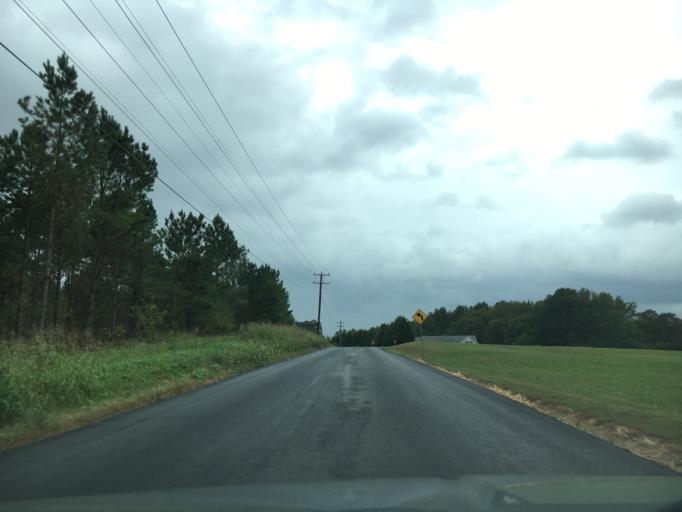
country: US
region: Virginia
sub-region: Amelia County
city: Amelia Court House
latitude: 37.3750
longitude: -77.9767
